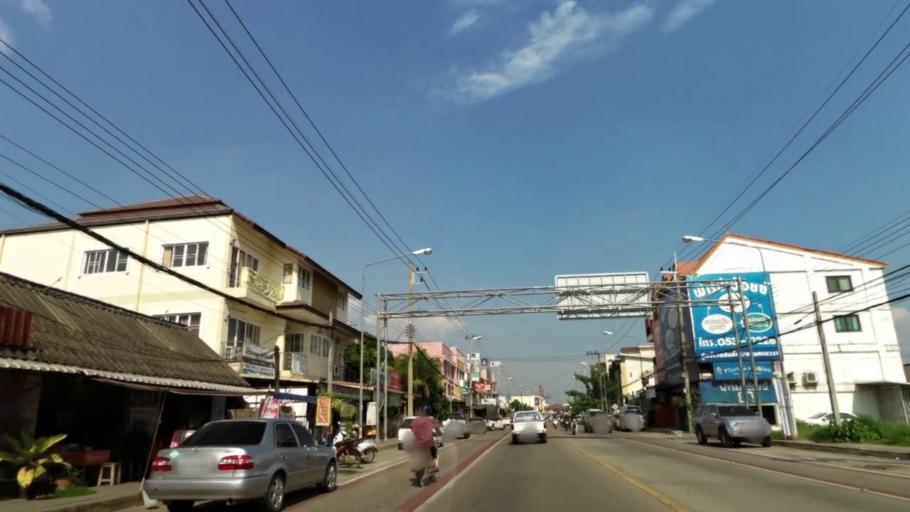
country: TH
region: Chiang Rai
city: Chiang Rai
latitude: 19.9224
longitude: 99.8341
